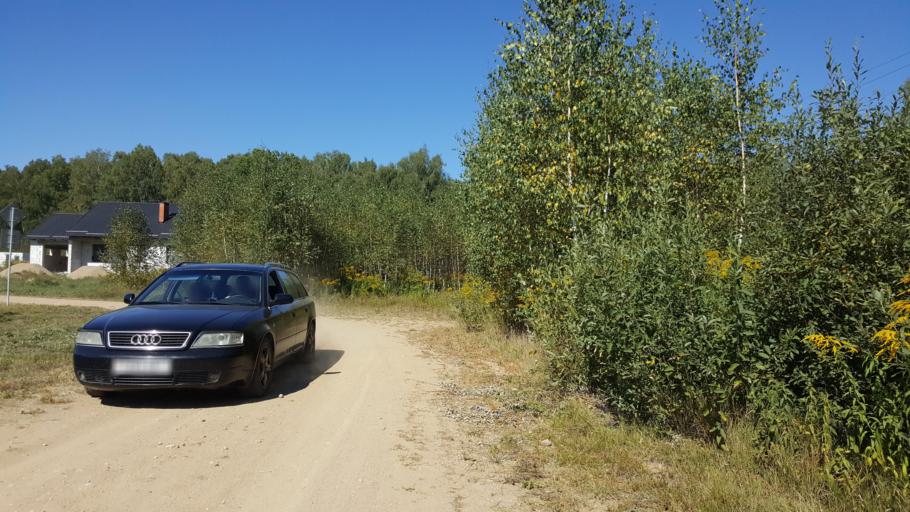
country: BY
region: Brest
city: Vysokaye
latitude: 52.2537
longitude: 23.4993
